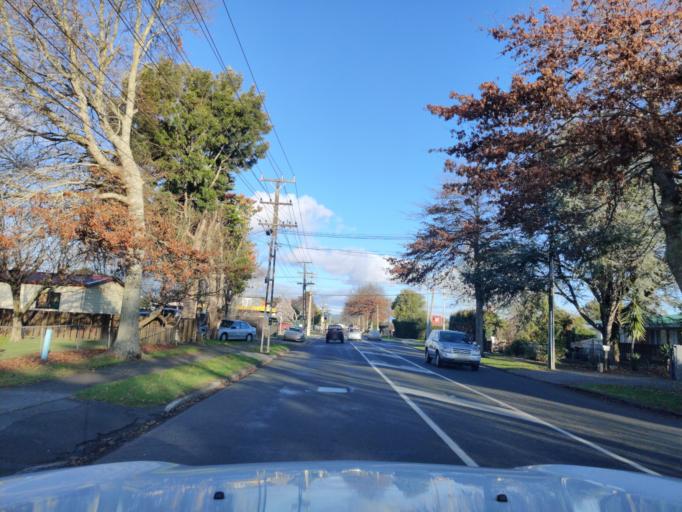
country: NZ
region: Auckland
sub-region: Auckland
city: Red Hill
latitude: -37.0516
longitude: 174.9568
